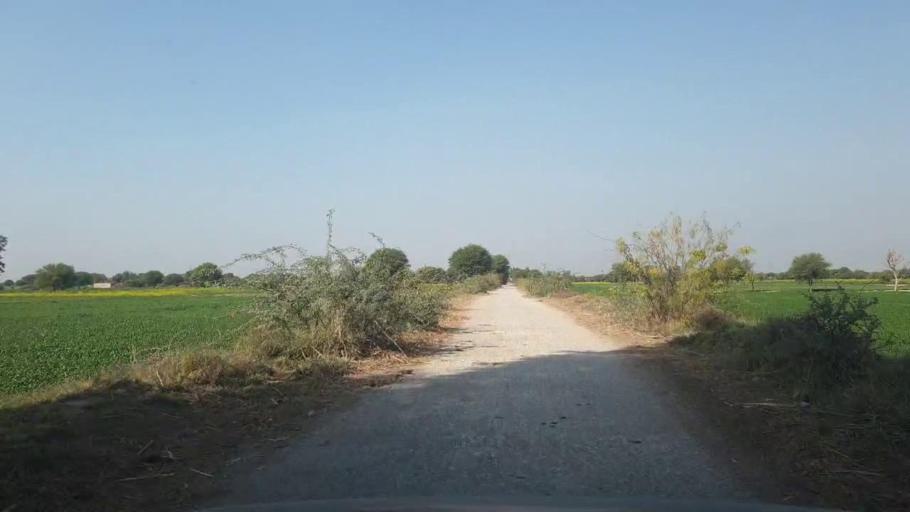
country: PK
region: Sindh
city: Chambar
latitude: 25.3046
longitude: 68.8457
